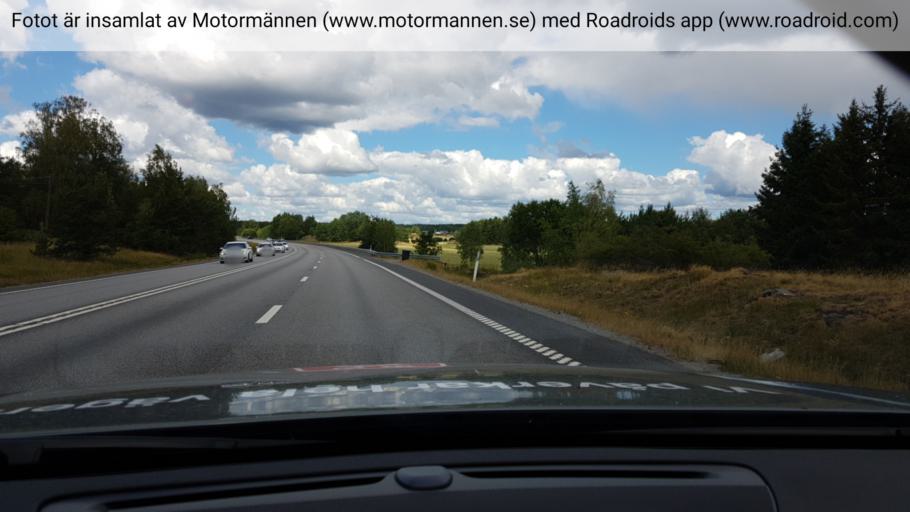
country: SE
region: Stockholm
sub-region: Osterakers Kommun
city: Akersberga
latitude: 59.4418
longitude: 18.2222
